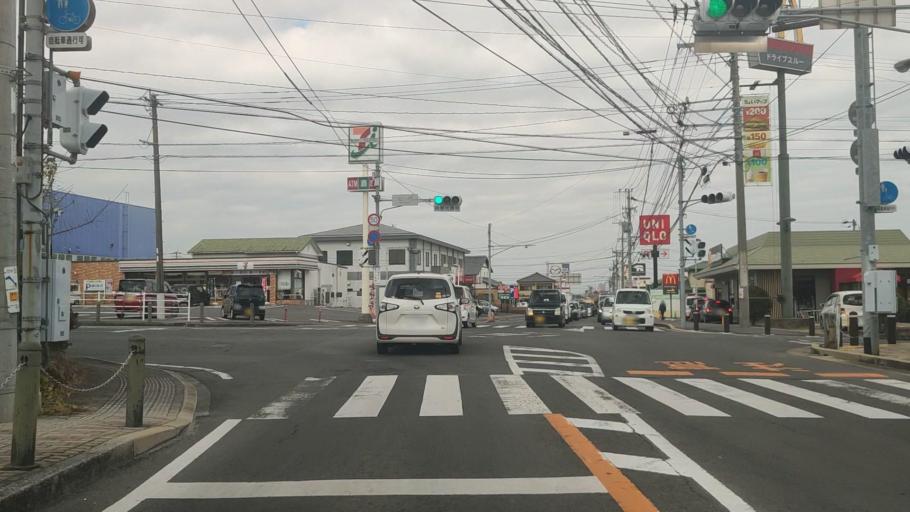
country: JP
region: Nagasaki
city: Shimabara
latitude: 32.8002
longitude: 130.3648
